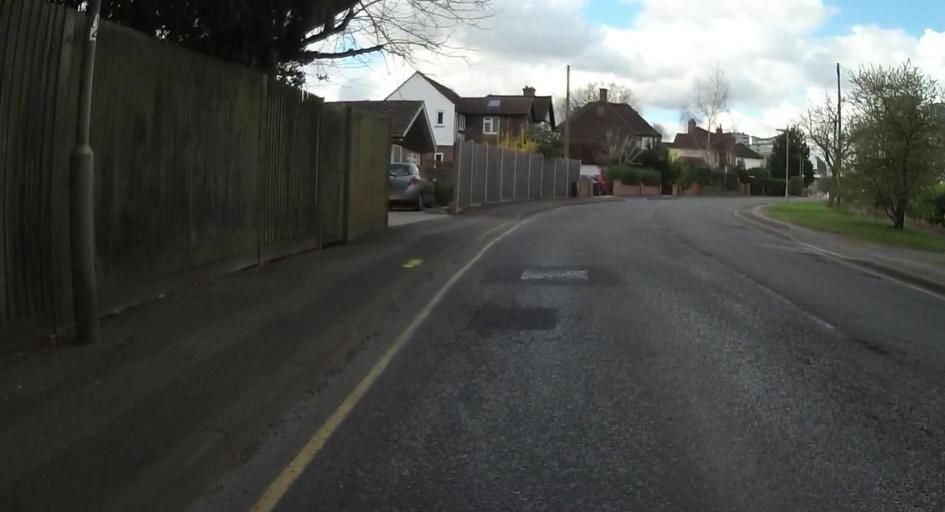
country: GB
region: England
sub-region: Surrey
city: Woking
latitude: 51.3189
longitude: -0.5525
